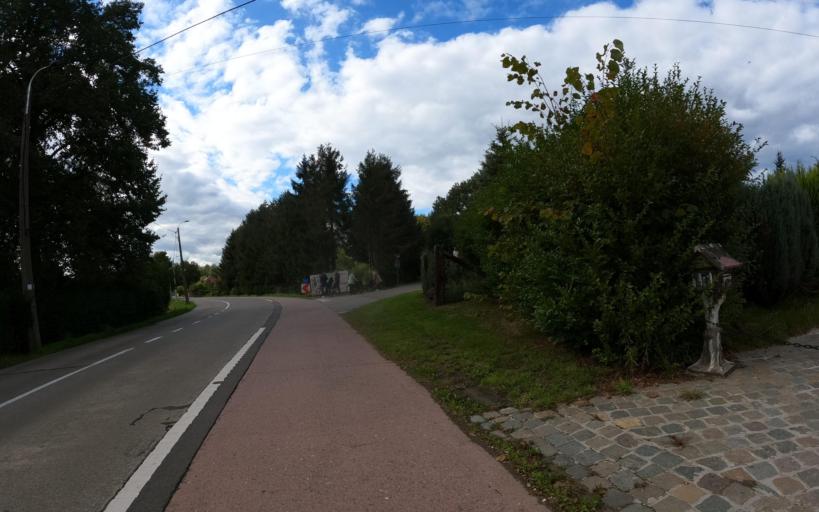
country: BE
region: Flanders
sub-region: Provincie Antwerpen
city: Heist-op-den-Berg
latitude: 51.0998
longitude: 4.7594
